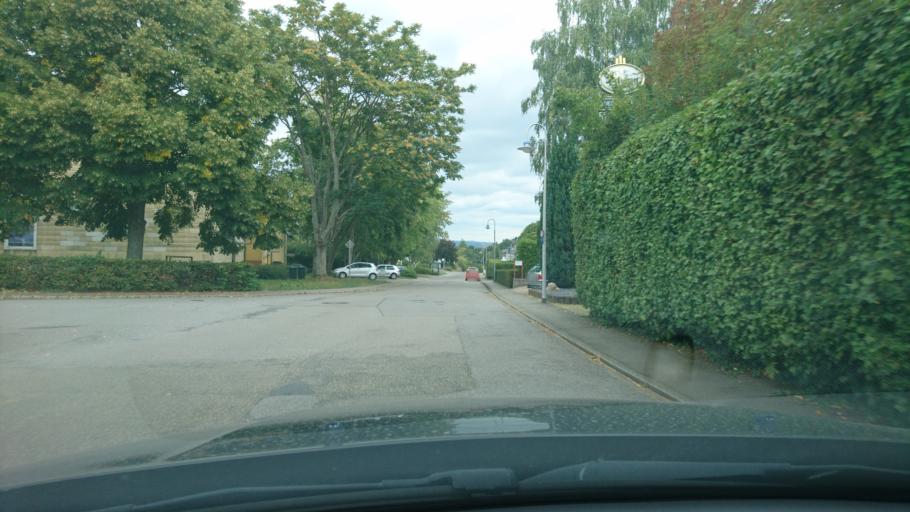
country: DE
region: Rheinland-Pfalz
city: Konz
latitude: 49.6885
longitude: 6.5720
